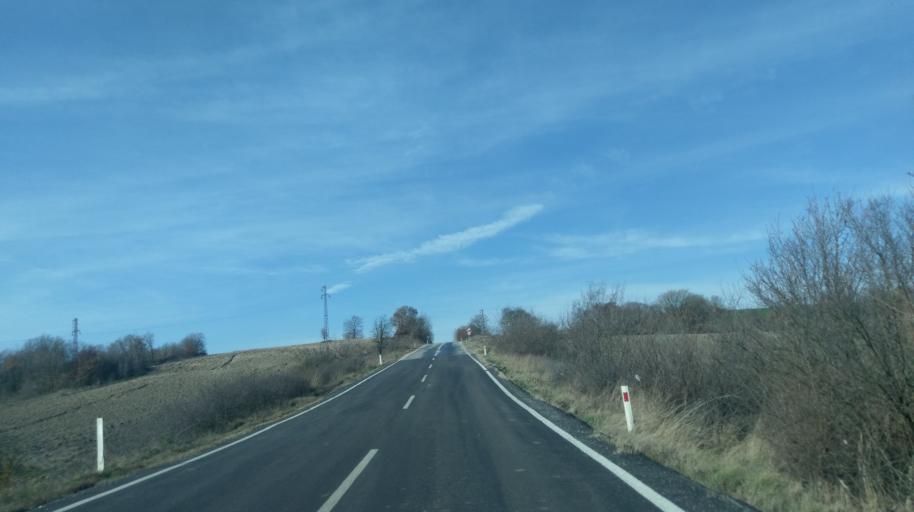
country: TR
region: Edirne
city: Copkoy
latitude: 41.2731
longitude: 26.7864
